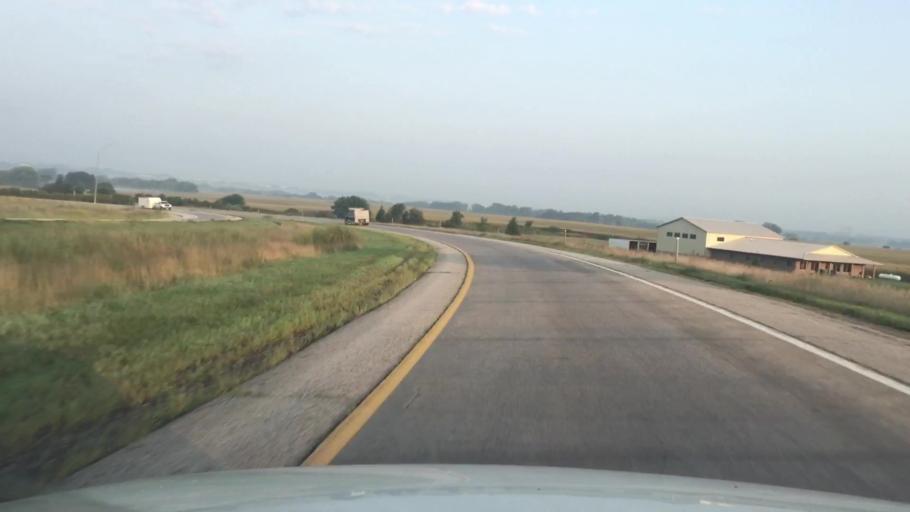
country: US
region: Iowa
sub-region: Polk County
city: Altoona
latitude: 41.6610
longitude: -93.5231
